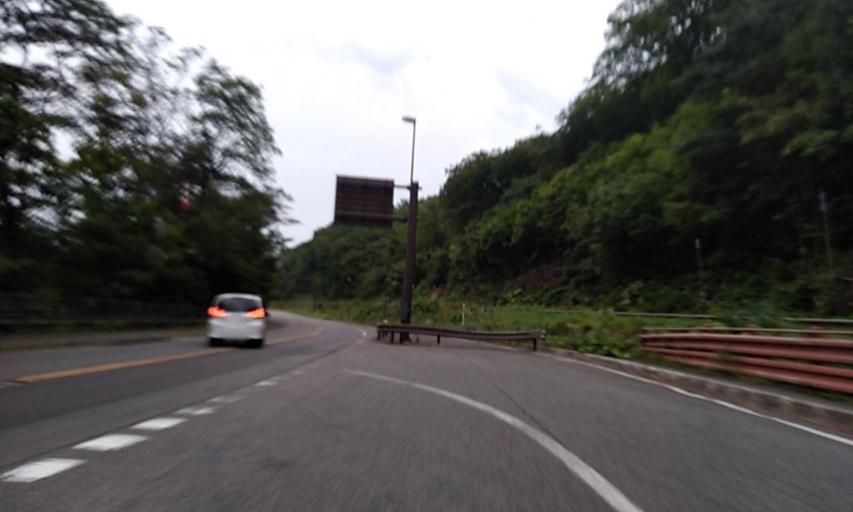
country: JP
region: Hokkaido
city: Abashiri
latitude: 44.0049
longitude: 144.2312
